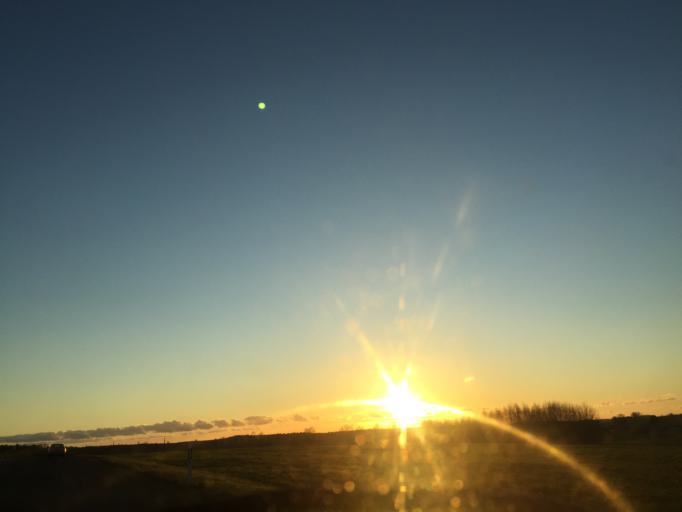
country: LV
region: Sigulda
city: Sigulda
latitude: 57.1699
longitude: 24.8134
